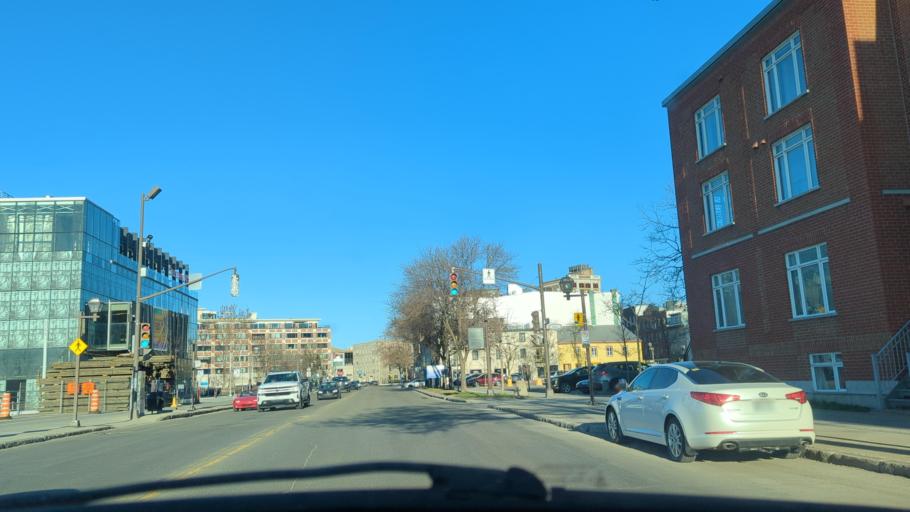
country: CA
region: Quebec
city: Quebec
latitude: 46.8171
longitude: -71.2067
